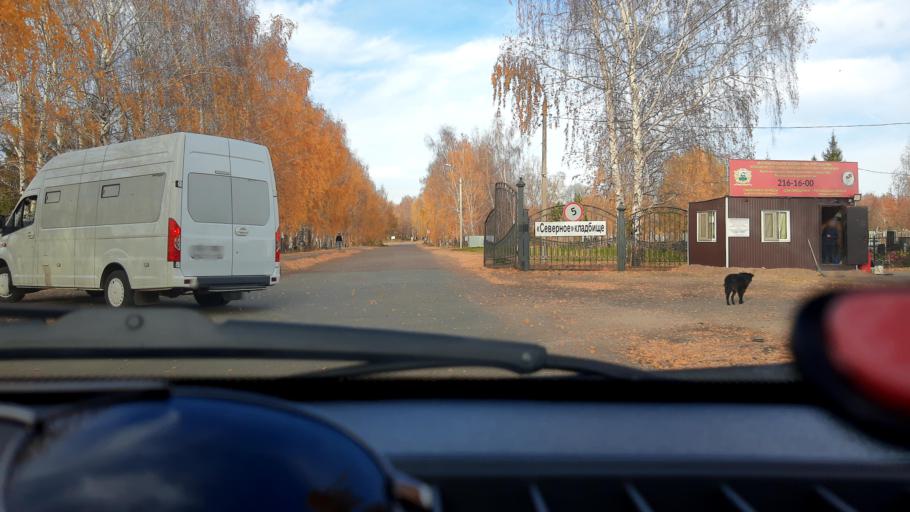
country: RU
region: Bashkortostan
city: Ufa
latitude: 54.8487
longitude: 56.1539
